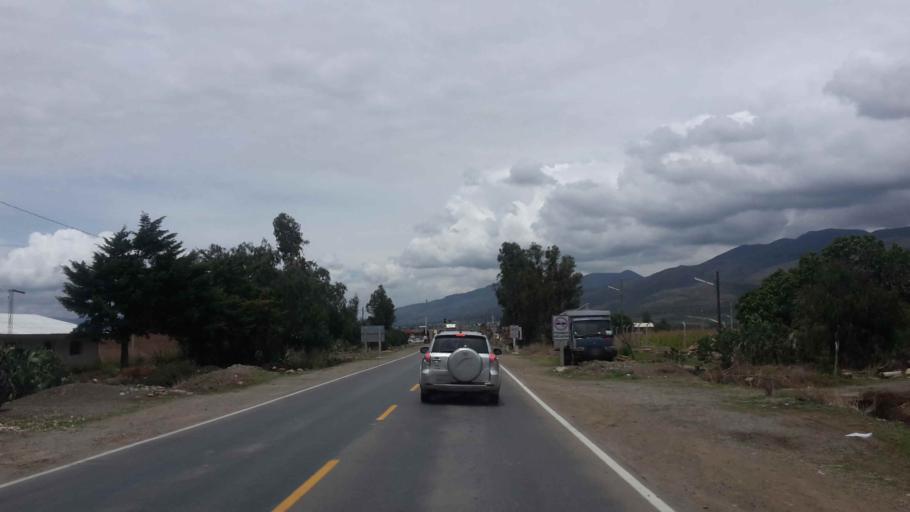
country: BO
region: Cochabamba
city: Punata
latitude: -17.5147
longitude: -65.8300
